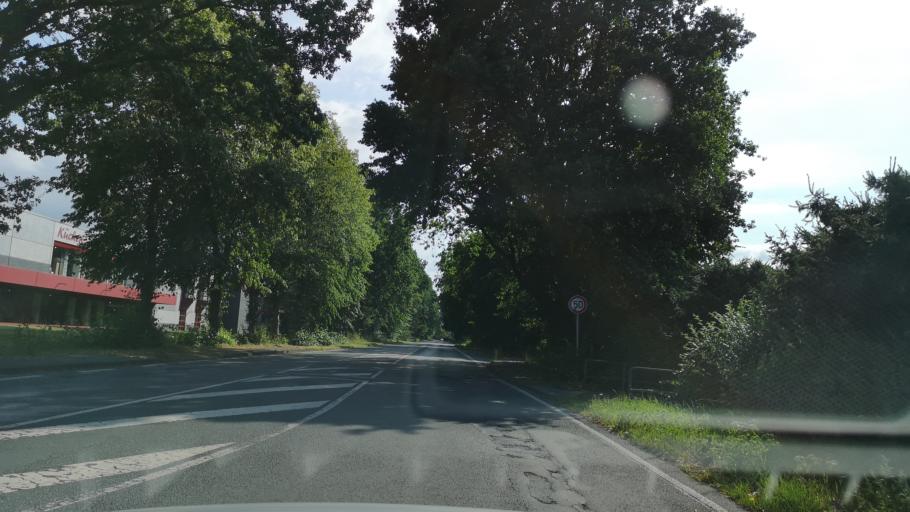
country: DE
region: North Rhine-Westphalia
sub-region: Regierungsbezirk Arnsberg
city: Holzwickede
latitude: 51.4608
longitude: 7.6176
